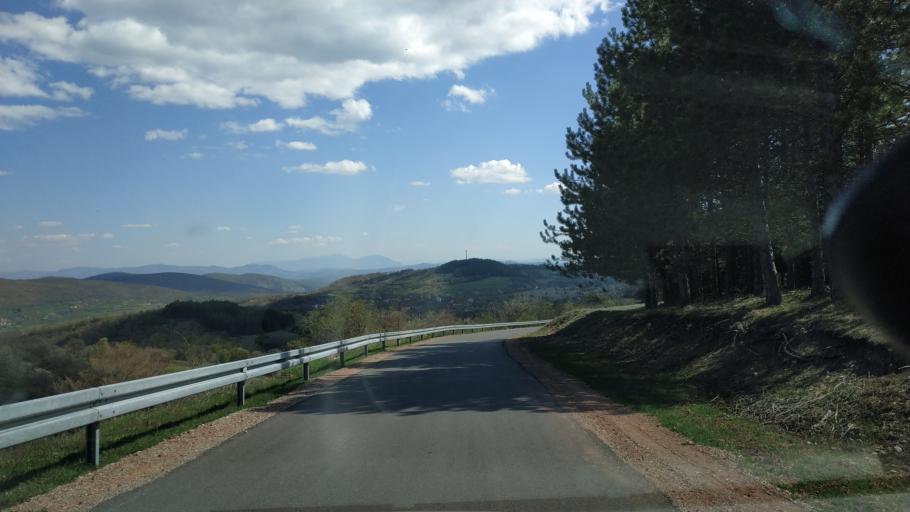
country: RS
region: Central Serbia
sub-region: Zajecarski Okrug
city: Soko Banja
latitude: 43.5798
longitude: 21.8952
